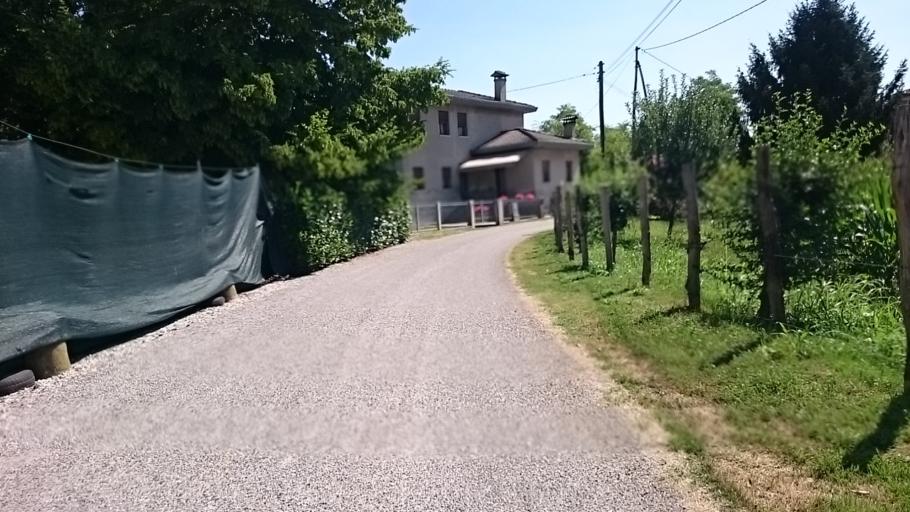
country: IT
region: Veneto
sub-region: Provincia di Padova
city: Cervarese Santa Croce
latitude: 45.4142
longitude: 11.7113
